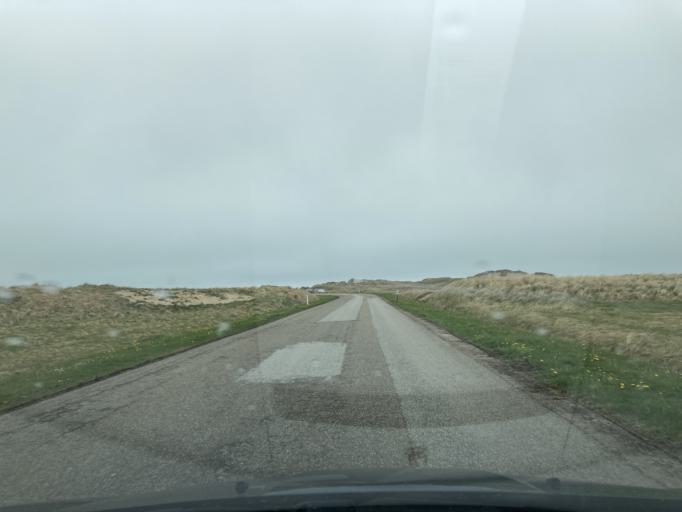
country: DK
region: North Denmark
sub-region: Thisted Kommune
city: Hanstholm
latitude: 57.0457
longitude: 8.5109
